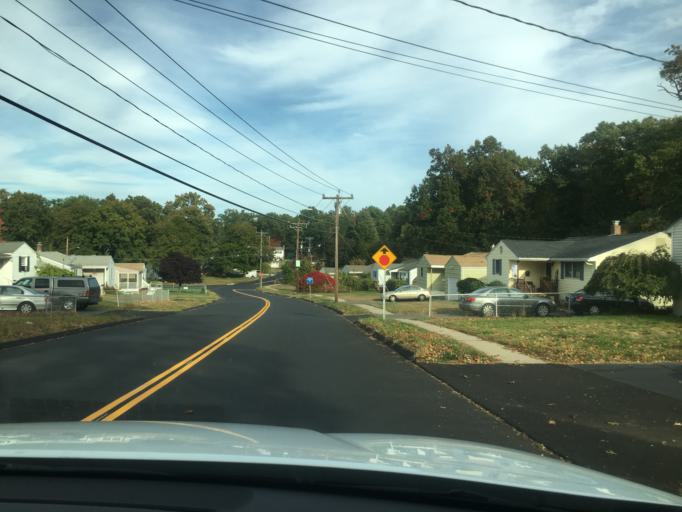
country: US
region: Connecticut
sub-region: Hartford County
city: Sherwood Manor
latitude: 42.0252
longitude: -72.5629
